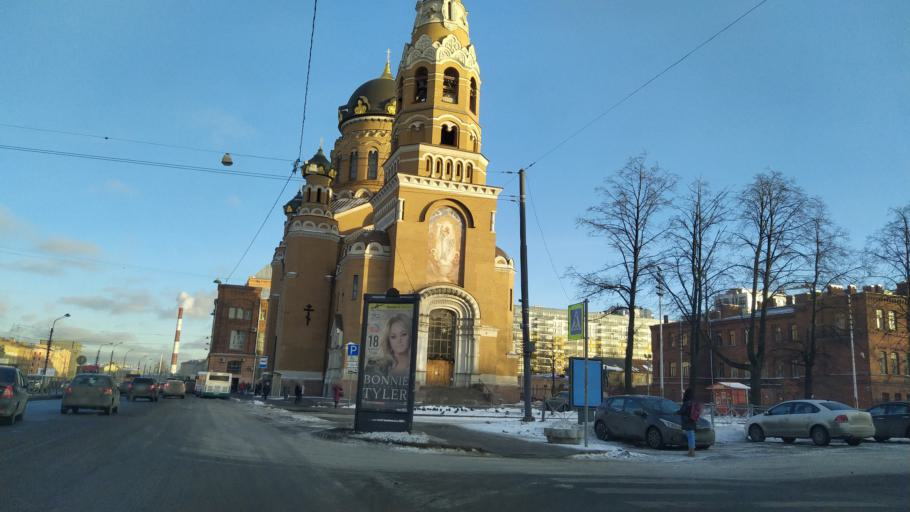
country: RU
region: St.-Petersburg
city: Admiralteisky
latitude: 59.9084
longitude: 30.3081
